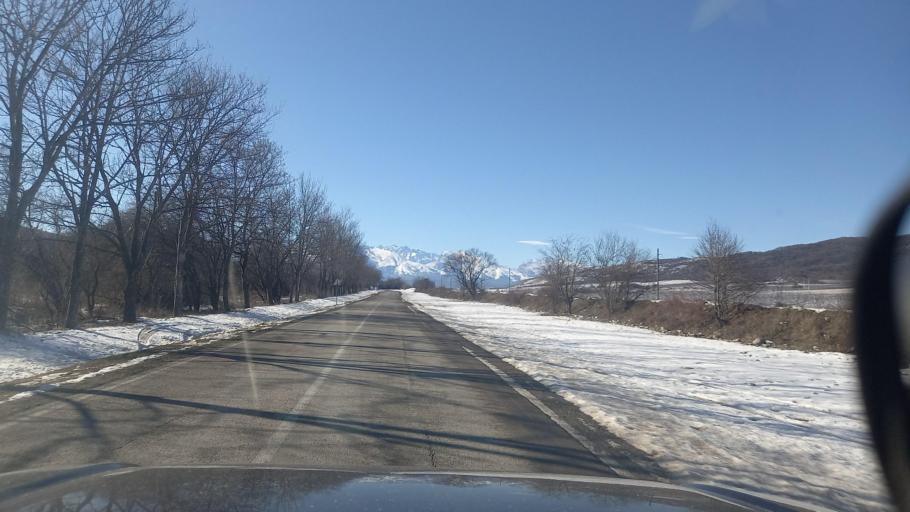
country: RU
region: North Ossetia
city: Chikola
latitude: 43.2469
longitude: 43.9636
